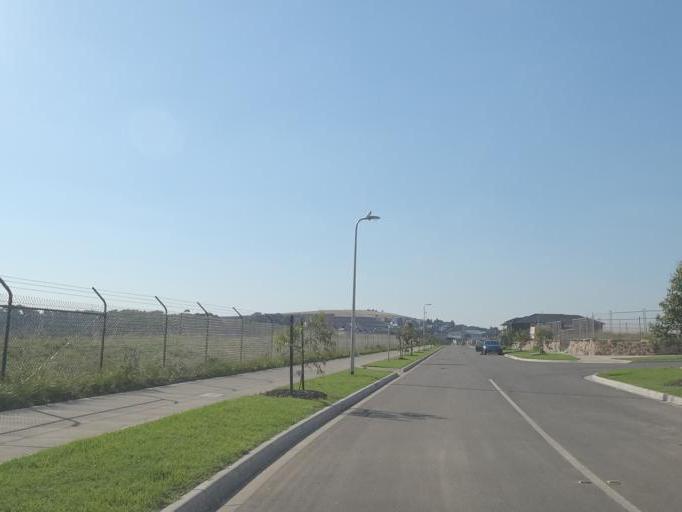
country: AU
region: Victoria
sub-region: Hume
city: Roxburgh Park
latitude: -37.6203
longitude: 144.9074
